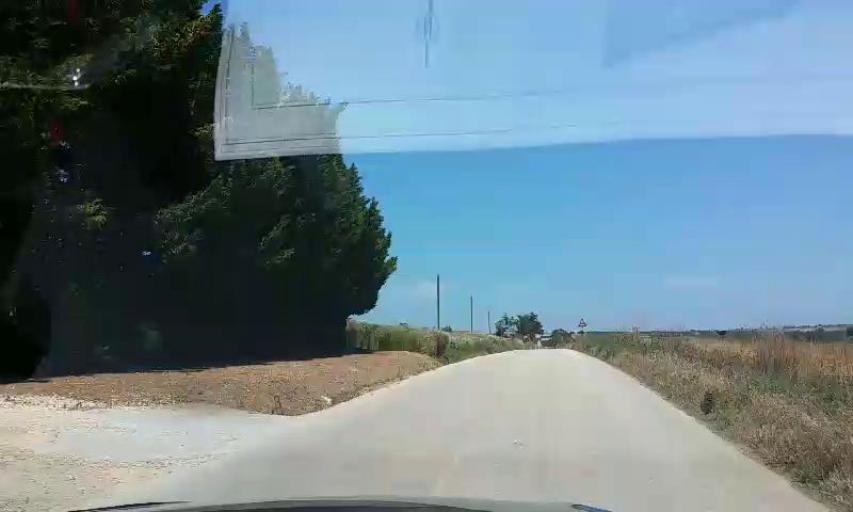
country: IT
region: Molise
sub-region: Provincia di Campobasso
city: San Giacomo degli Schiavoni
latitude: 41.9649
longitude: 14.9004
